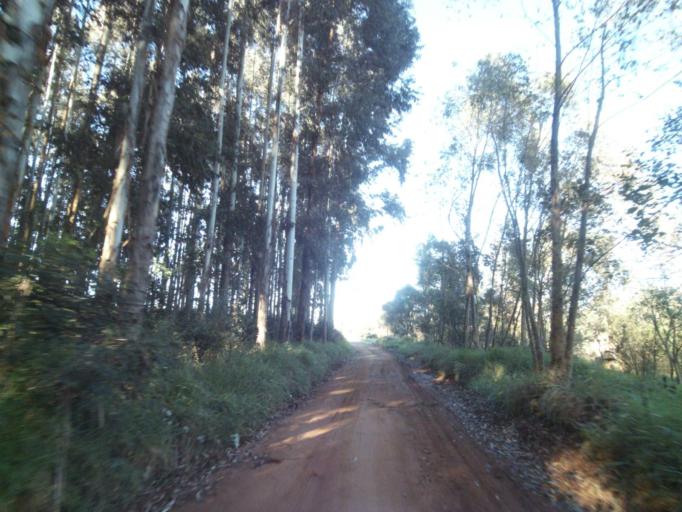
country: BR
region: Parana
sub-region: Tibagi
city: Tibagi
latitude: -24.5444
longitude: -50.3672
